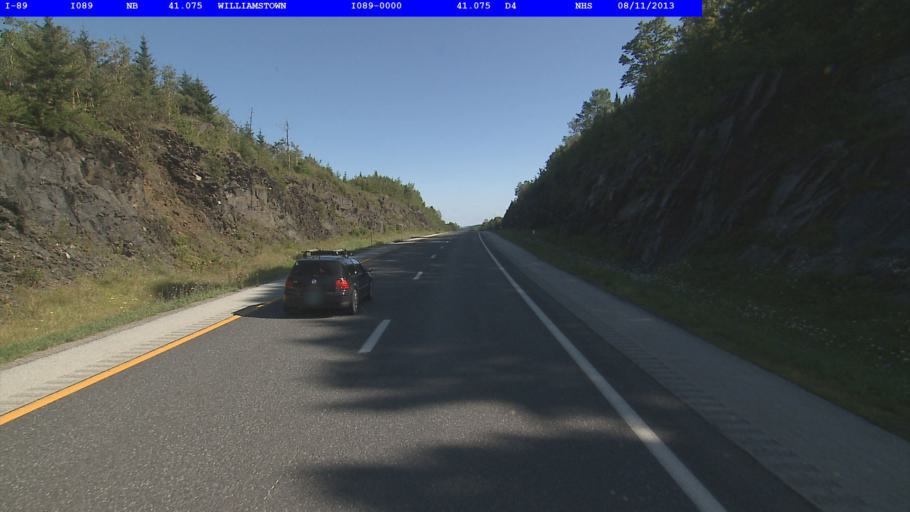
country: US
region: Vermont
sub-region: Washington County
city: Northfield
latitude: 44.0886
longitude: -72.6134
